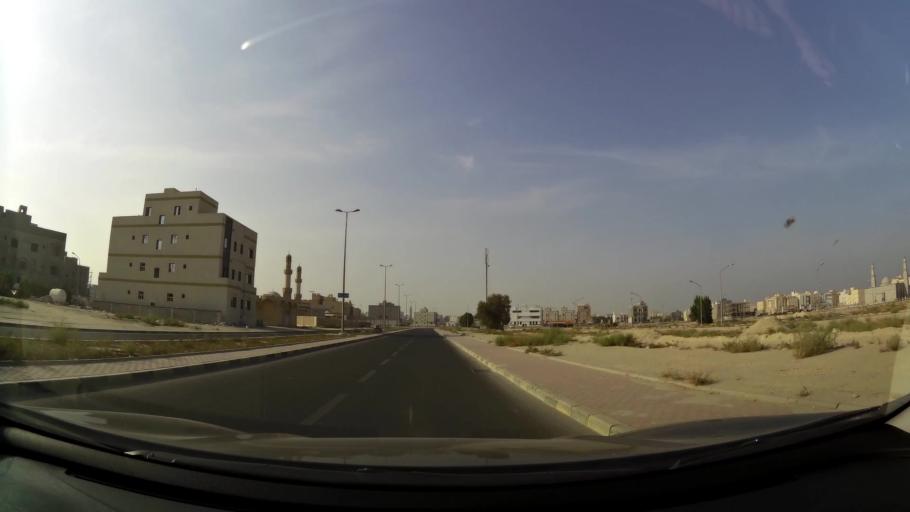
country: KW
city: Al Funaytis
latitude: 29.2061
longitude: 48.1002
